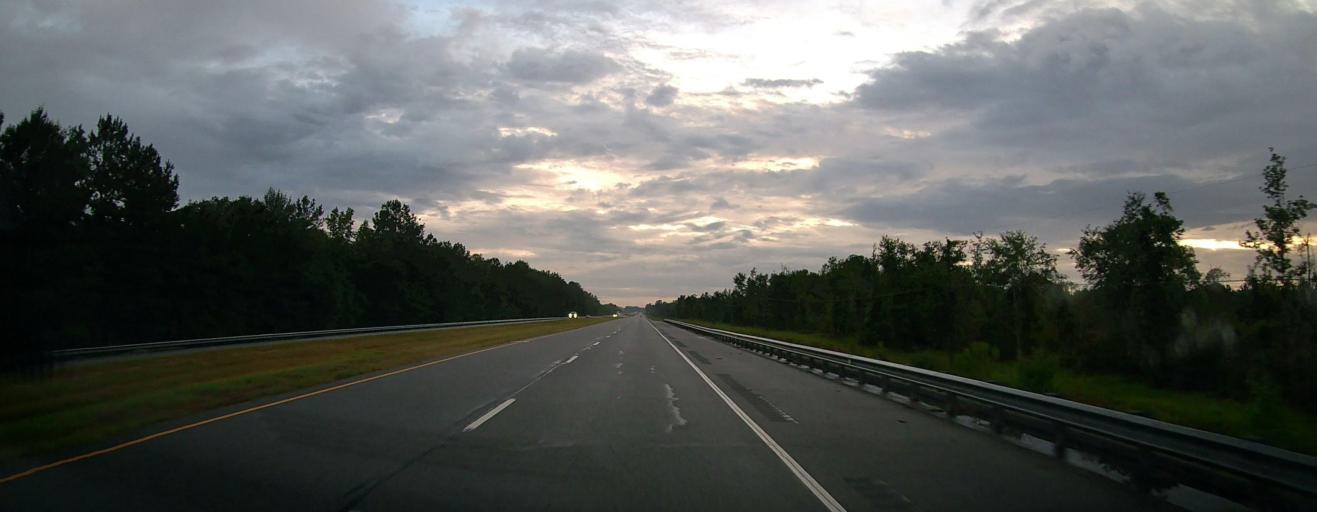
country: US
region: Georgia
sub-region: Lanier County
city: Lakeland
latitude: 30.9298
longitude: -83.0236
